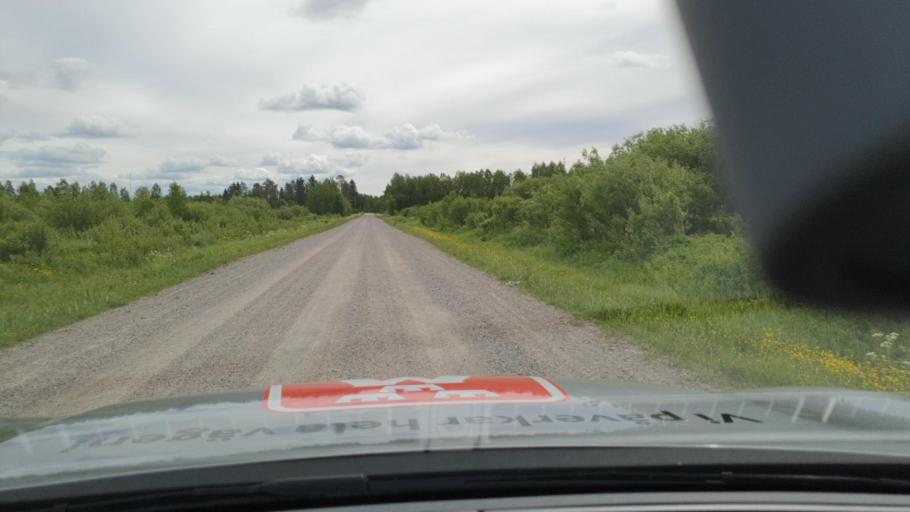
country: SE
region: Norrbotten
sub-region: Haparanda Kommun
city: Haparanda
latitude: 65.9492
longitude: 23.7861
